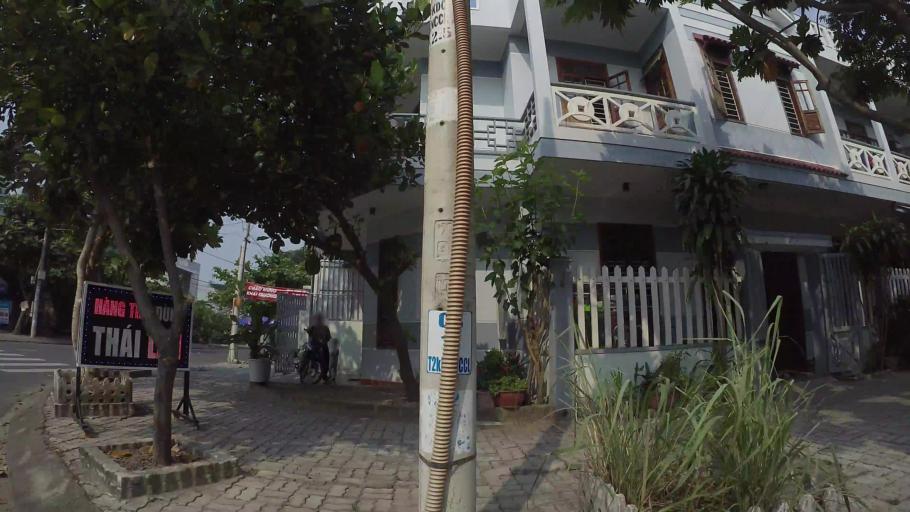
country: VN
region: Da Nang
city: Cam Le
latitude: 15.9965
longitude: 108.2132
